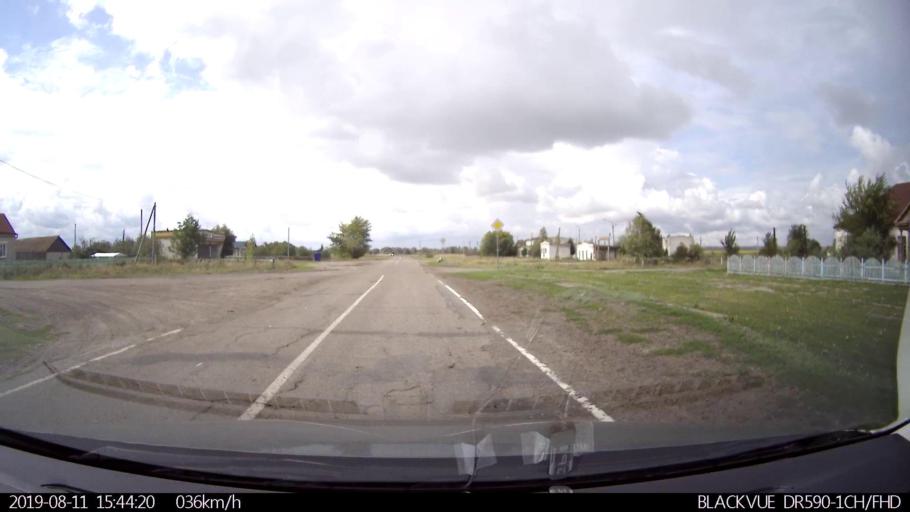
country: RU
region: Ulyanovsk
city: Ignatovka
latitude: 53.8813
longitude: 47.6570
